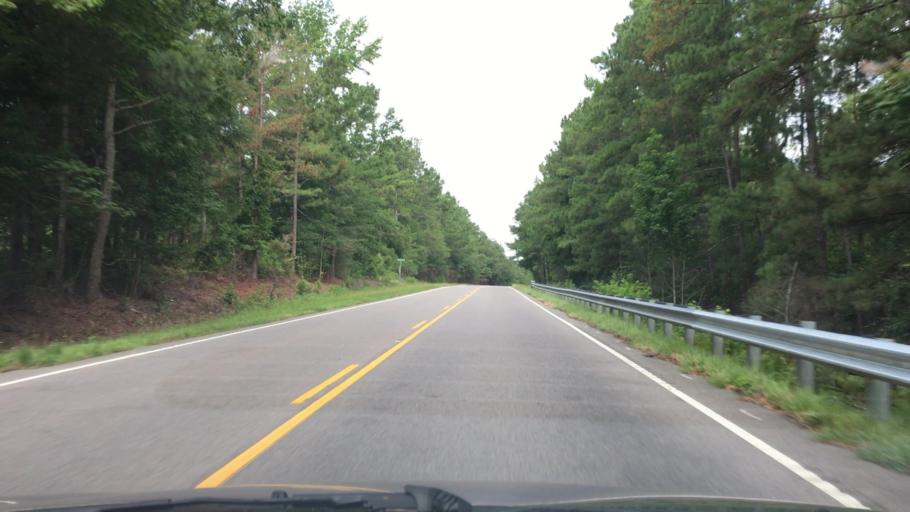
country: US
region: South Carolina
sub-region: Lexington County
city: Leesville
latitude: 33.6761
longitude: -81.4319
